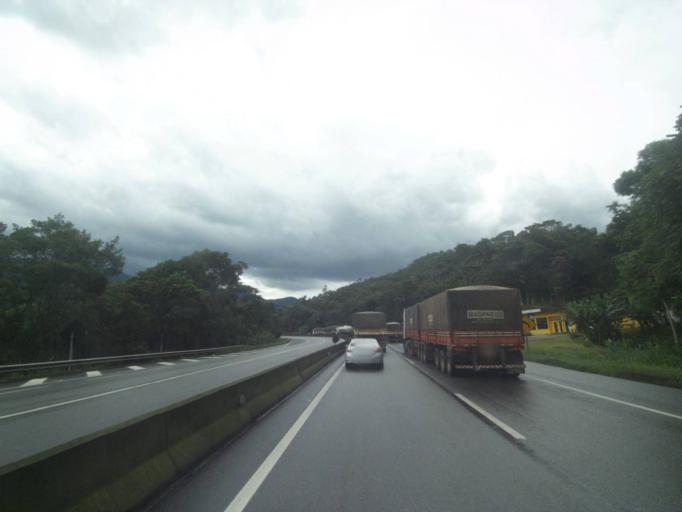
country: BR
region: Parana
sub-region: Antonina
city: Antonina
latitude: -25.5681
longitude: -48.8122
